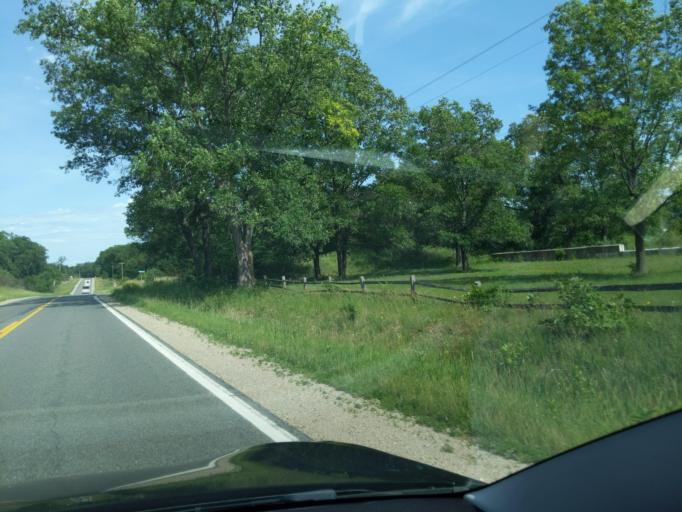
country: US
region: Michigan
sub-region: Muskegon County
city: Whitehall
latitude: 43.4097
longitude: -86.2979
